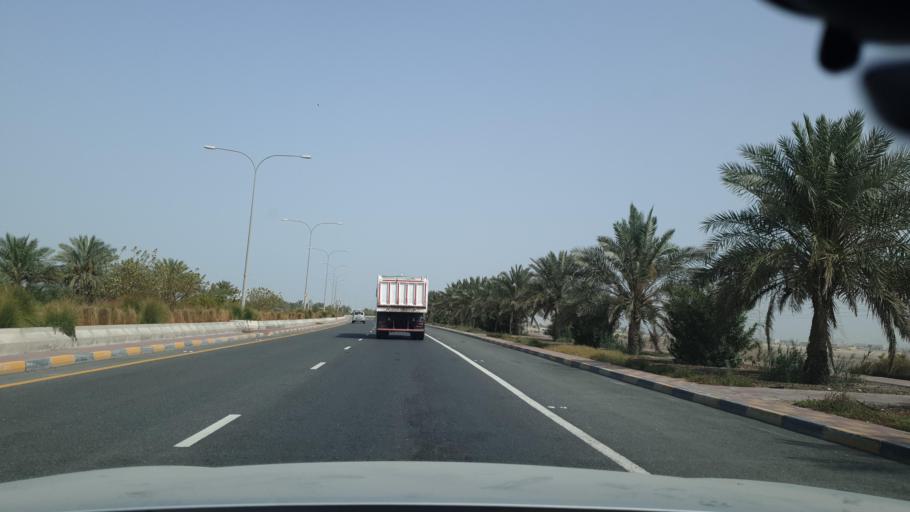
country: QA
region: Al Wakrah
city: Umm Sa'id
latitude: 25.0120
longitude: 51.5550
